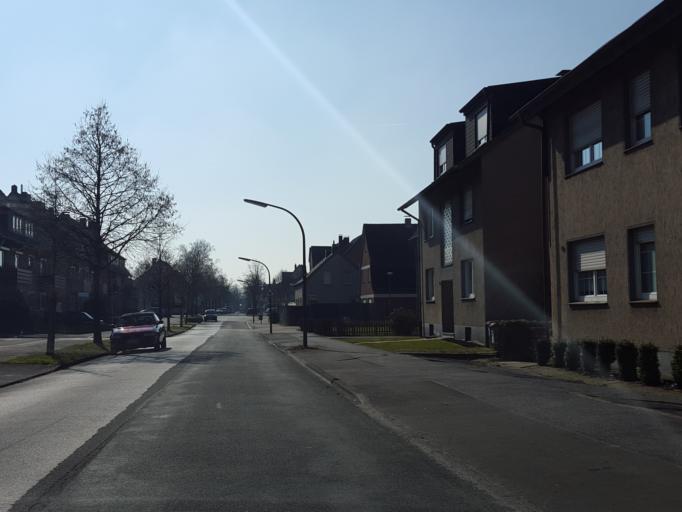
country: DE
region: North Rhine-Westphalia
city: Oer-Erkenschwick
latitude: 51.6521
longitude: 7.2471
